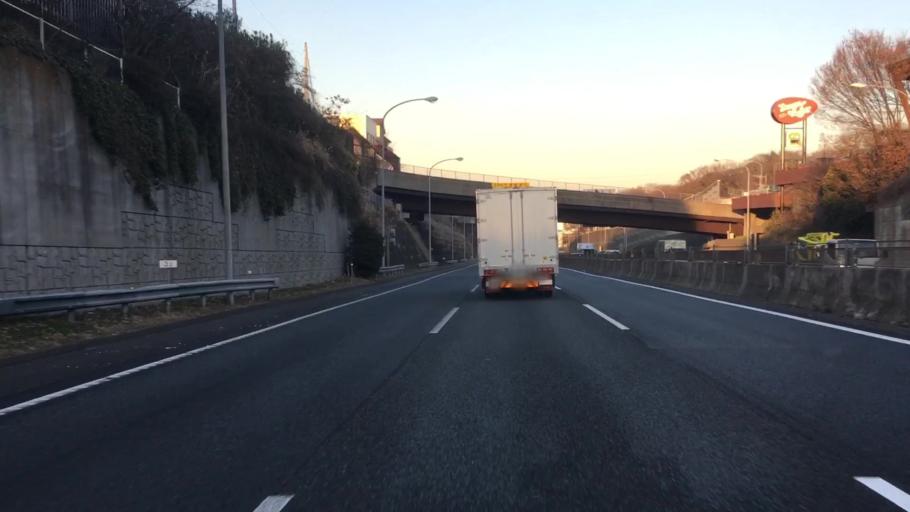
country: JP
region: Kanagawa
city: Yokohama
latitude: 35.4558
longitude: 139.5819
